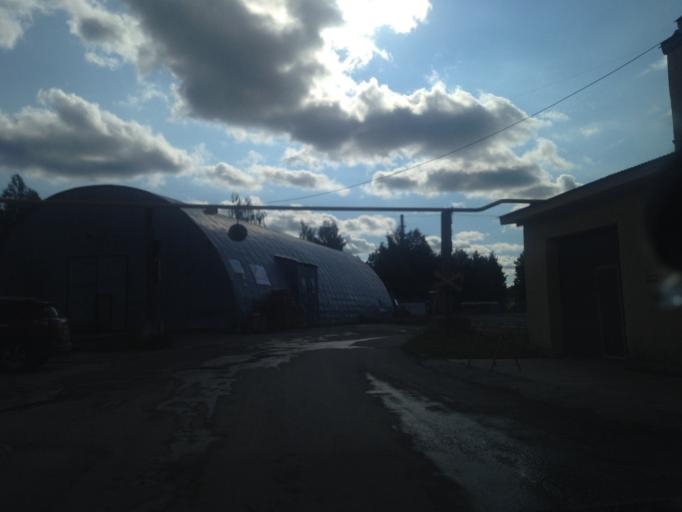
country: RU
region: Sverdlovsk
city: Yekaterinburg
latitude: 56.9110
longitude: 60.6345
